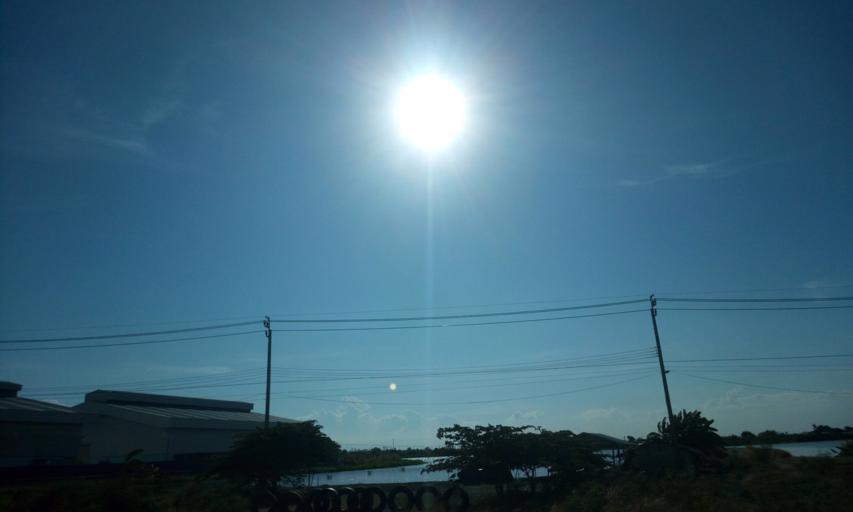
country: TH
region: Samut Prakan
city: Bang Bo District
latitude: 13.5413
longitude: 100.7507
